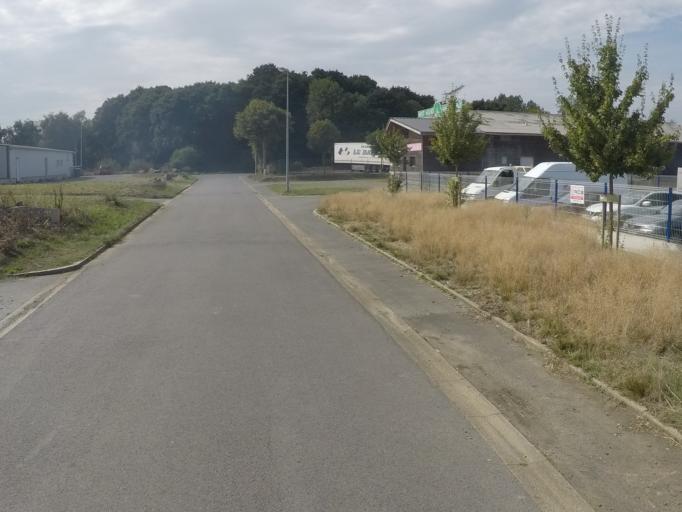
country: FR
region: Brittany
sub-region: Departement des Cotes-d'Armor
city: Lanvollon
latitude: 48.6407
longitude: -2.9897
